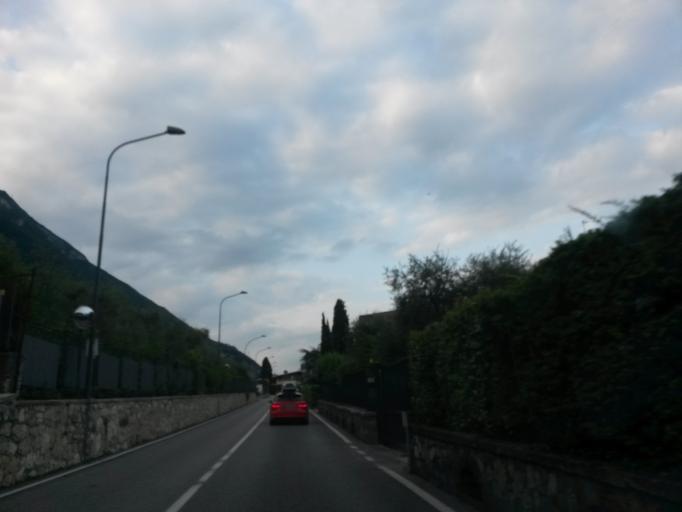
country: IT
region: Lombardy
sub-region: Provincia di Brescia
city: Gargnano
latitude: 45.6912
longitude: 10.6652
